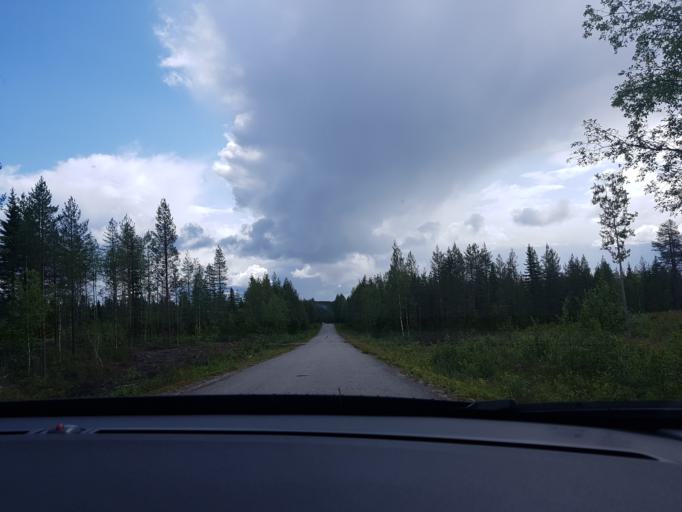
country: FI
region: Kainuu
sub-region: Kehys-Kainuu
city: Kuhmo
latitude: 64.4558
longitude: 29.6520
